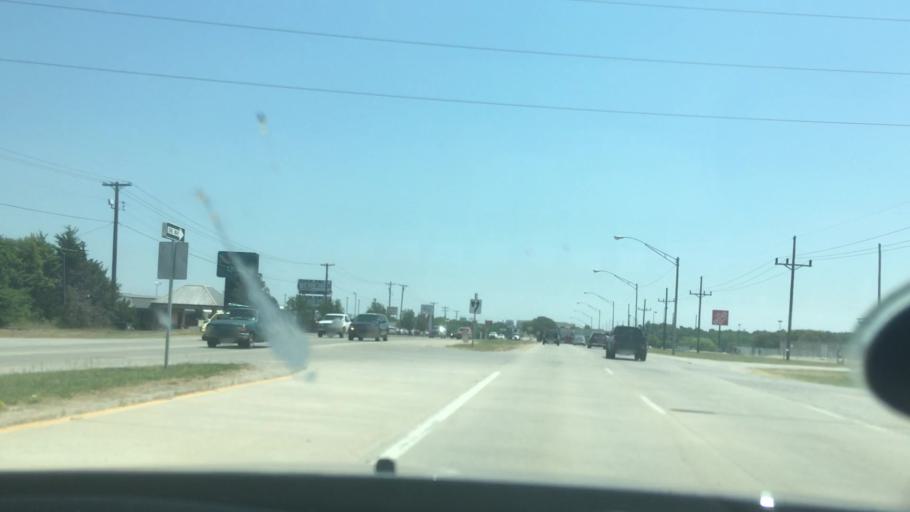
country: US
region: Oklahoma
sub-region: Pontotoc County
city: Ada
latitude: 34.7897
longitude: -96.6754
